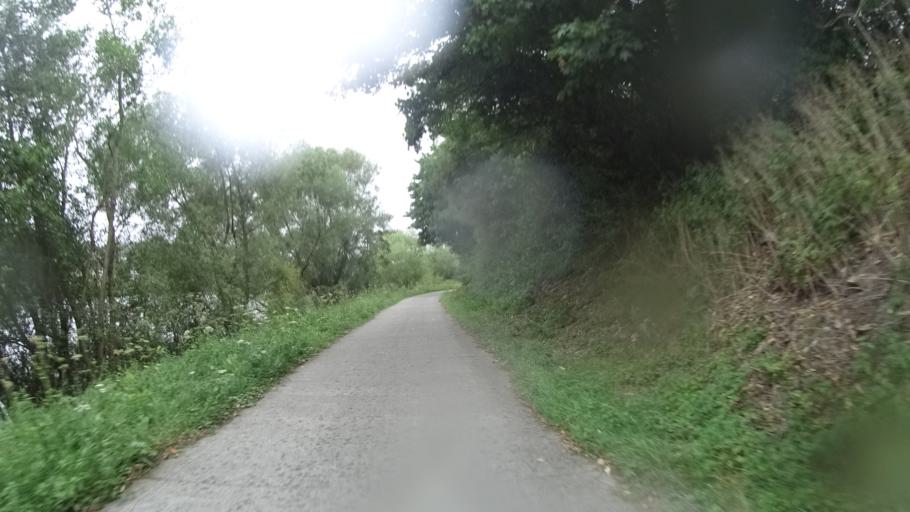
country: BE
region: Wallonia
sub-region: Province de Liege
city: Wanze
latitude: 50.5231
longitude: 5.1966
